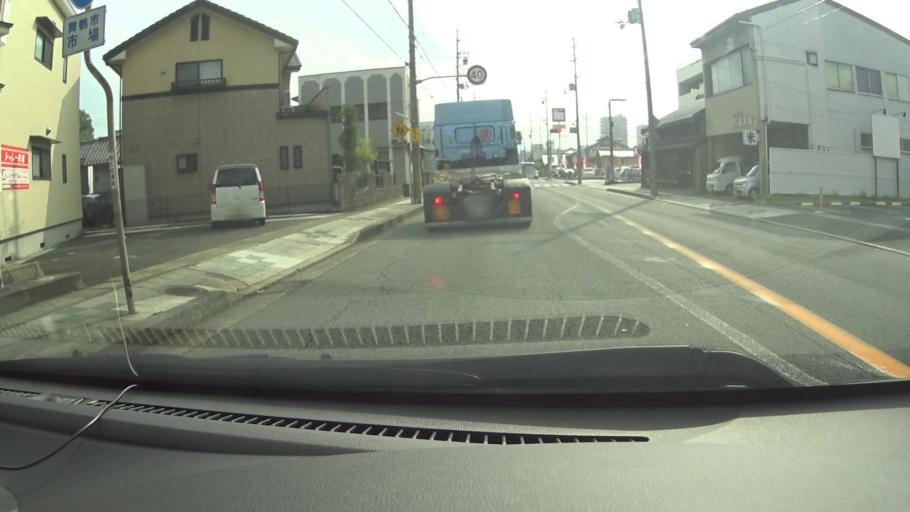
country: JP
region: Kyoto
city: Kameoka
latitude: 35.0813
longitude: 135.5113
